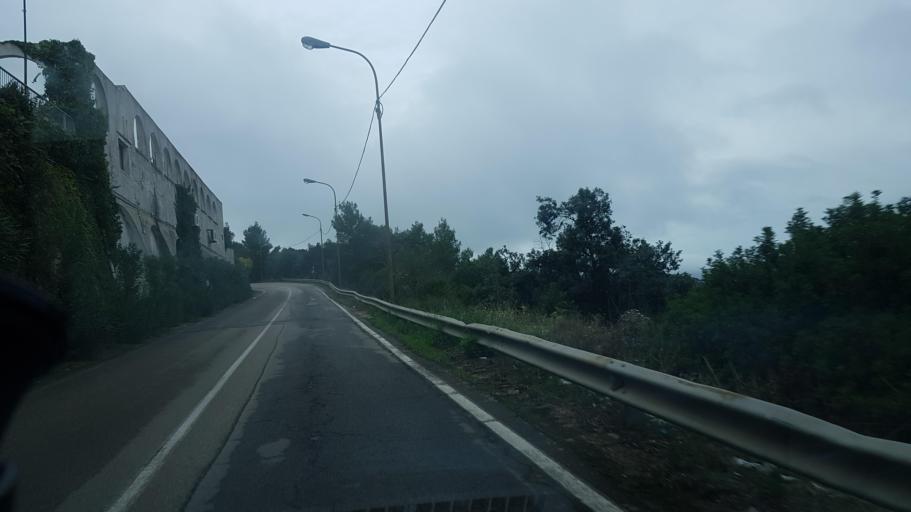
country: IT
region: Apulia
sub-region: Provincia di Brindisi
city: Ostuni
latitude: 40.7324
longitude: 17.5573
